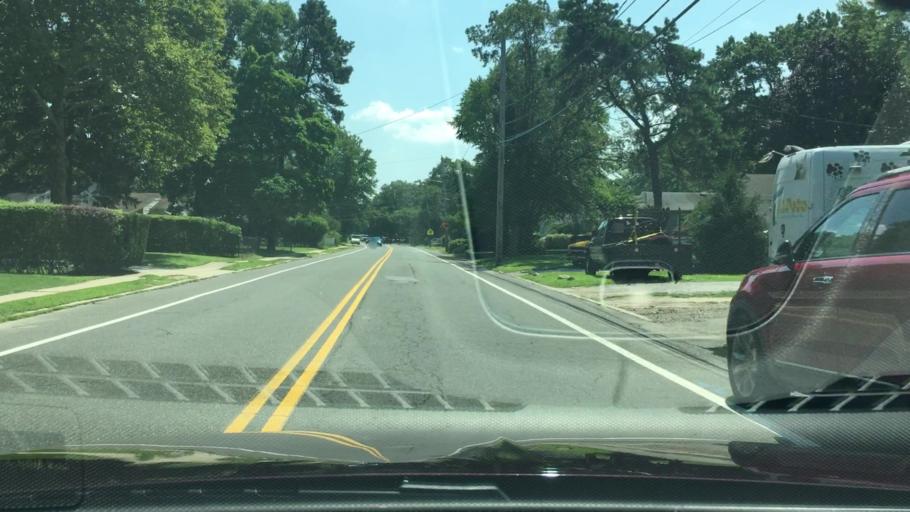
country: US
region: New York
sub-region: Suffolk County
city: Bay Wood
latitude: 40.7546
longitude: -73.2927
